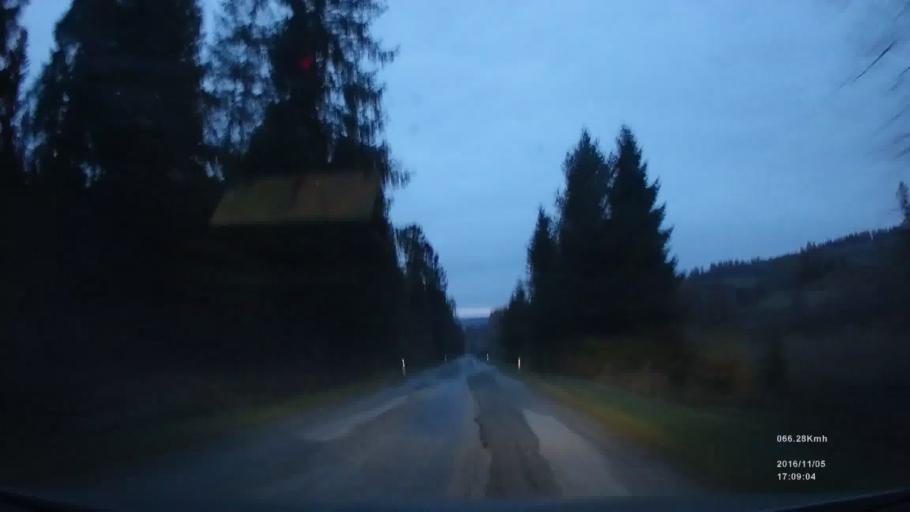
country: SK
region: Presovsky
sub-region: Okres Presov
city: Levoca
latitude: 49.0511
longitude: 20.5175
